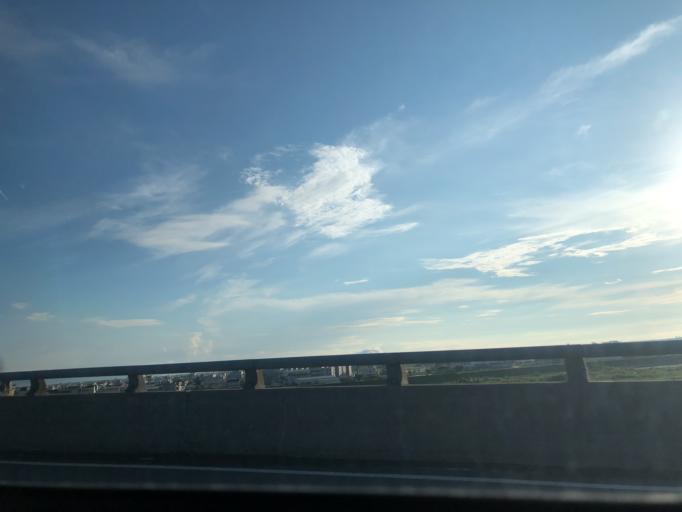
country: TW
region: Taiwan
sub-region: Yilan
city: Yilan
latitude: 24.7572
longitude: 121.7782
